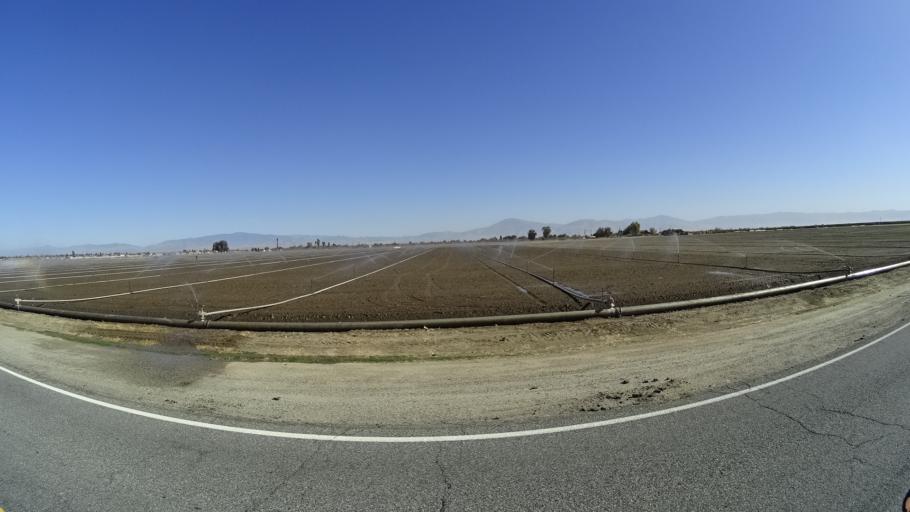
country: US
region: California
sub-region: Kern County
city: Greenfield
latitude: 35.2619
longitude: -119.0567
